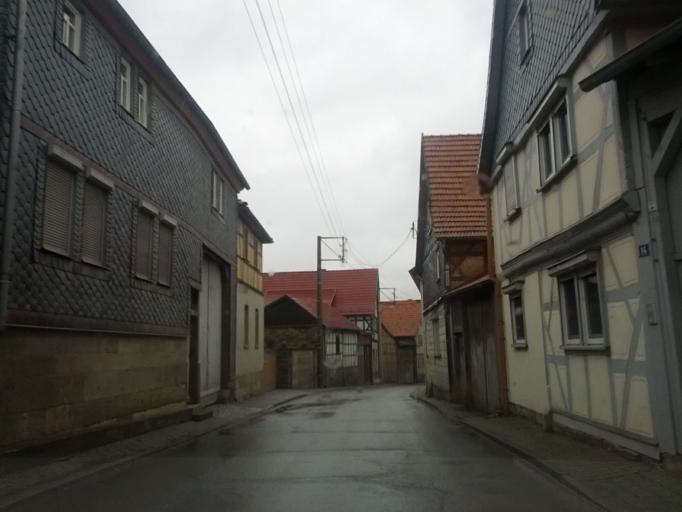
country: DE
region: Thuringia
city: Oberdorla
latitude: 51.1661
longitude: 10.4207
